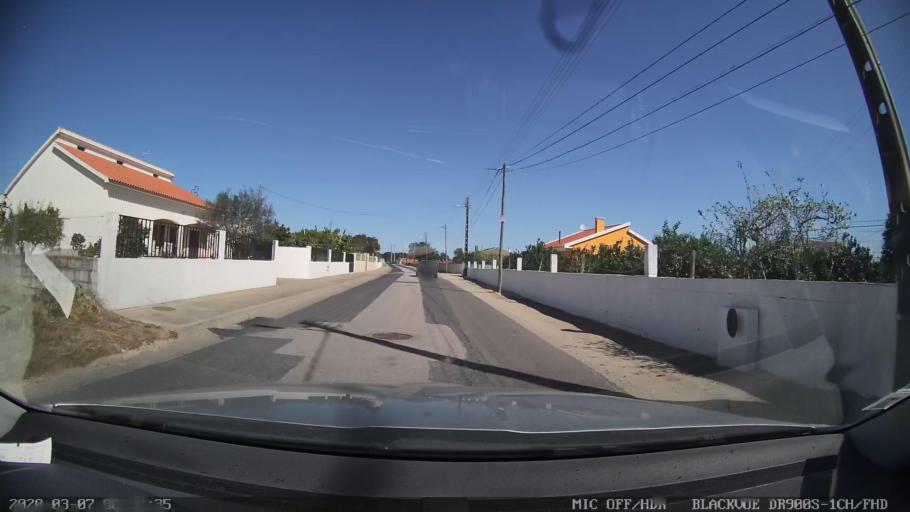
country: PT
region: Santarem
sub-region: Benavente
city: Benavente
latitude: 38.9528
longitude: -8.8191
